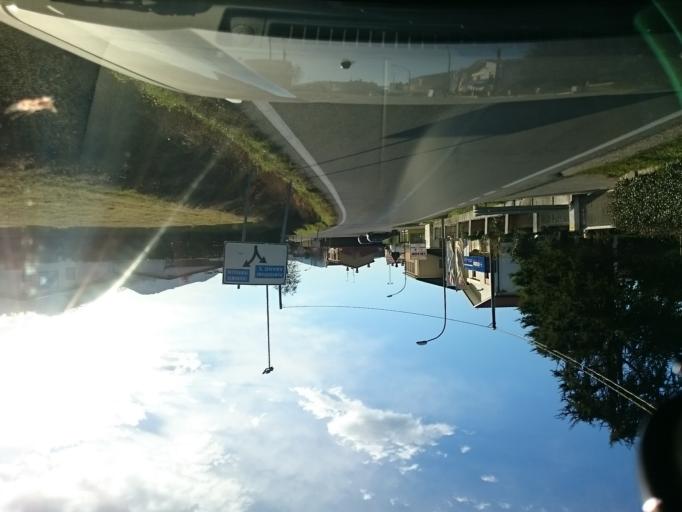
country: IT
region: Veneto
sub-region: Provincia di Padova
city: San Biagio
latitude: 45.3560
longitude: 11.7443
